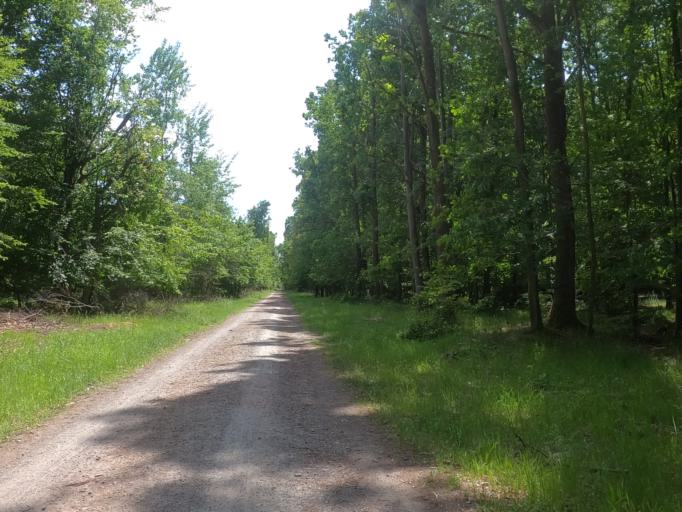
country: DE
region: Hesse
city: Morfelden-Walldorf
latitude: 49.9791
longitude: 8.5434
